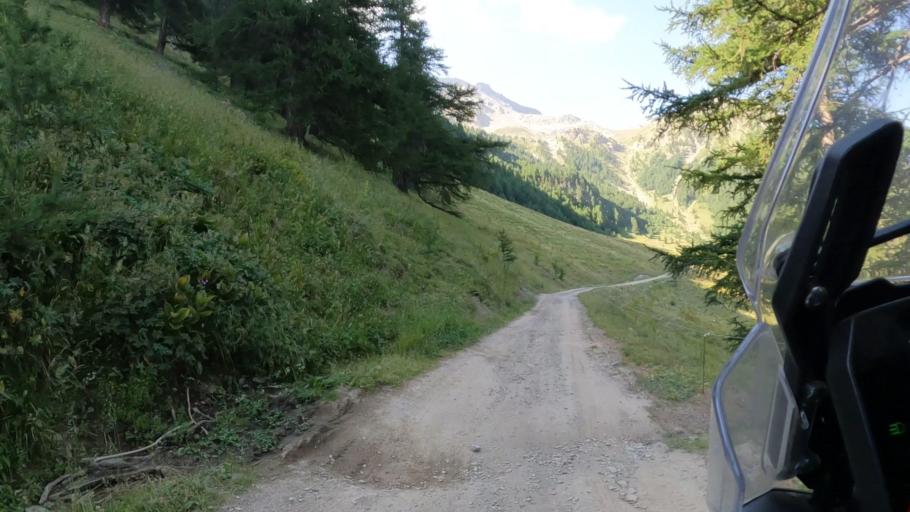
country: FR
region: Provence-Alpes-Cote d'Azur
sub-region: Departement des Hautes-Alpes
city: Guillestre
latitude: 44.5891
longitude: 6.6244
